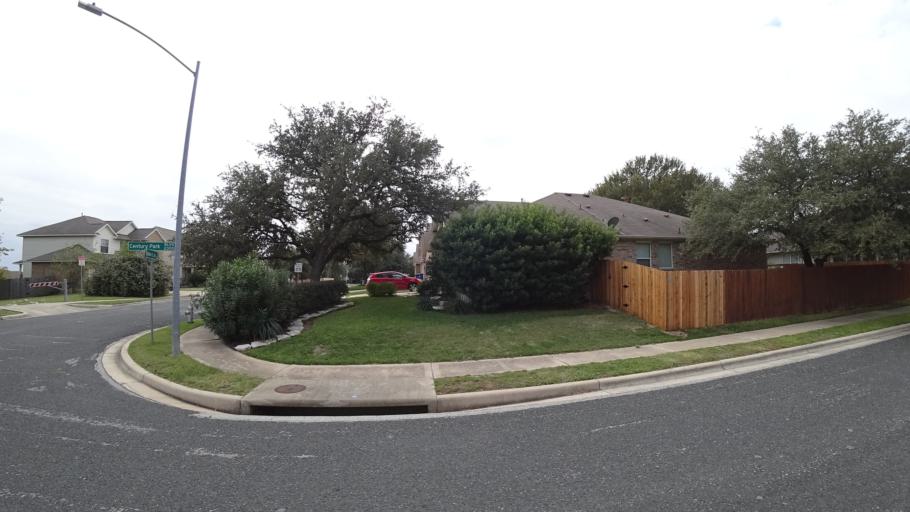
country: US
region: Texas
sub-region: Travis County
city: Wells Branch
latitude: 30.4318
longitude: -97.6899
